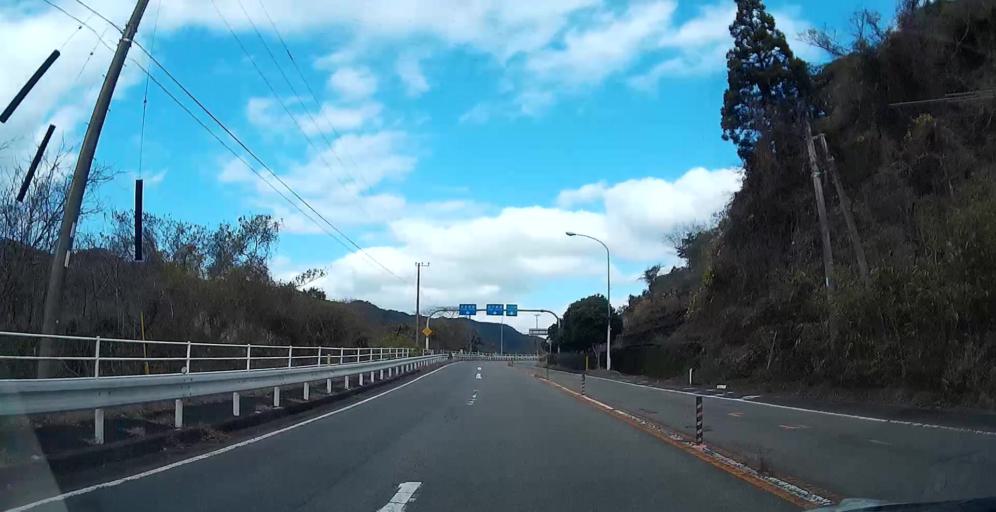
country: JP
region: Kumamoto
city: Yatsushiro
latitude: 32.3661
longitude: 130.5163
